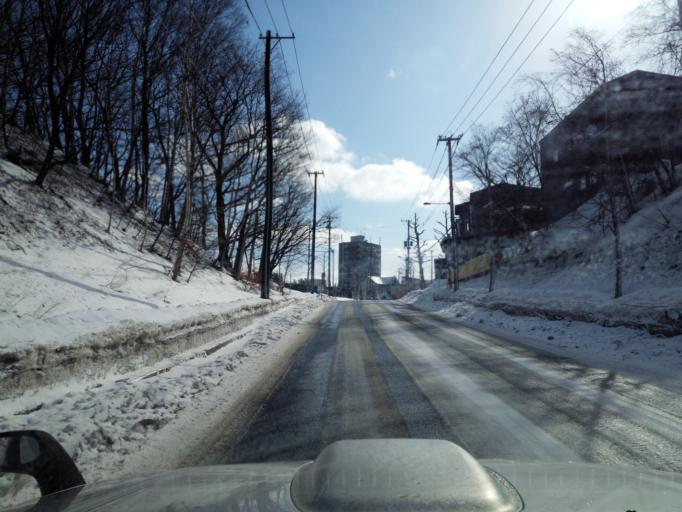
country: JP
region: Hokkaido
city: Sapporo
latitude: 42.9868
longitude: 141.4435
